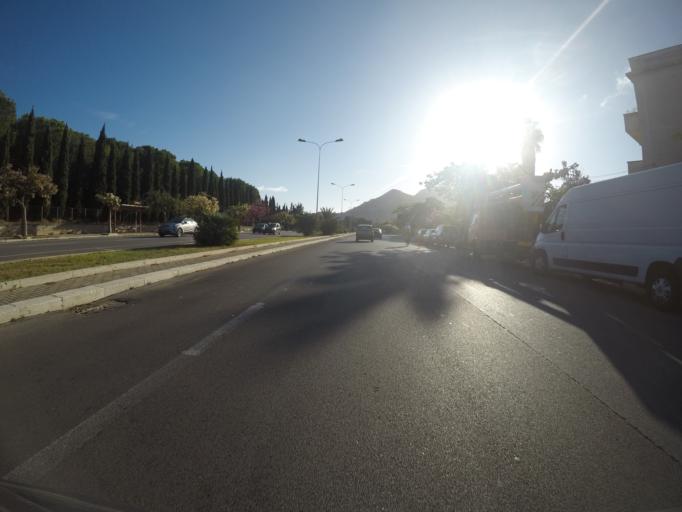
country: IT
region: Sicily
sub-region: Palermo
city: Palermo
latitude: 38.1889
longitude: 13.3121
